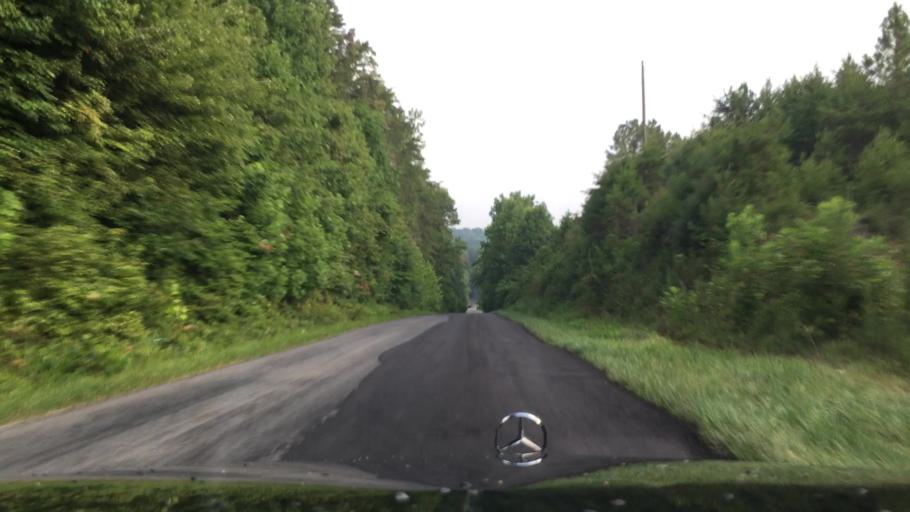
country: US
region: Virginia
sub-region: Campbell County
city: Timberlake
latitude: 37.2436
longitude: -79.3018
